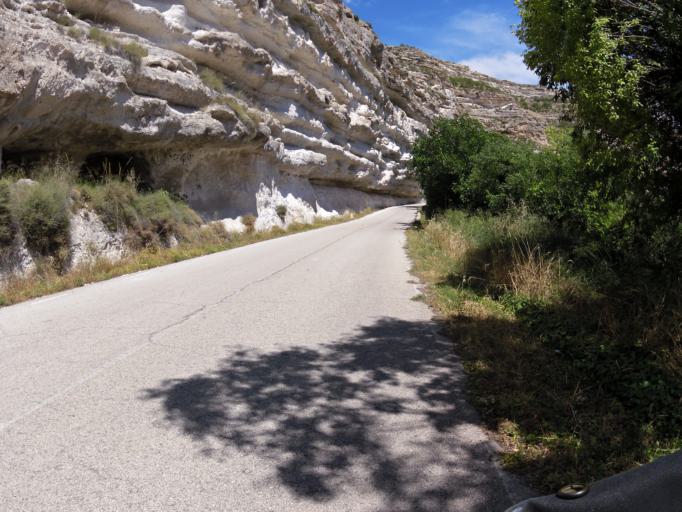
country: ES
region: Castille-La Mancha
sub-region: Provincia de Albacete
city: Jorquera
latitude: 39.1794
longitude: -1.5319
